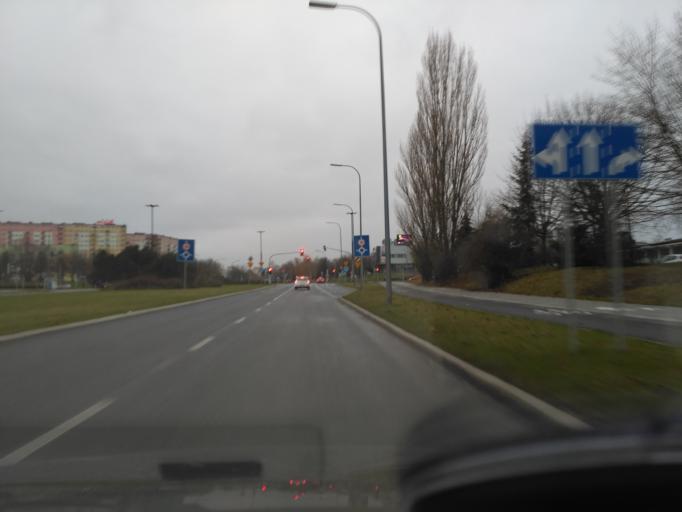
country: PL
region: Lublin Voivodeship
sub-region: Powiat lubelski
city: Lublin
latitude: 51.2613
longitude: 22.5526
